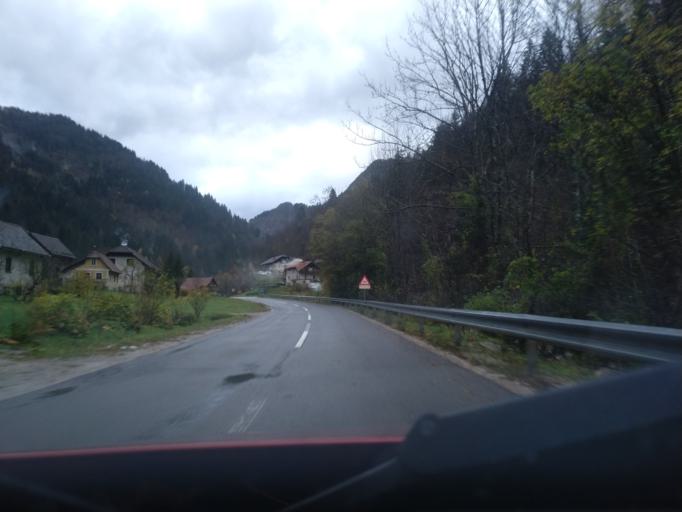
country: SI
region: Solcava
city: Solcava
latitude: 46.4198
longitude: 14.6771
